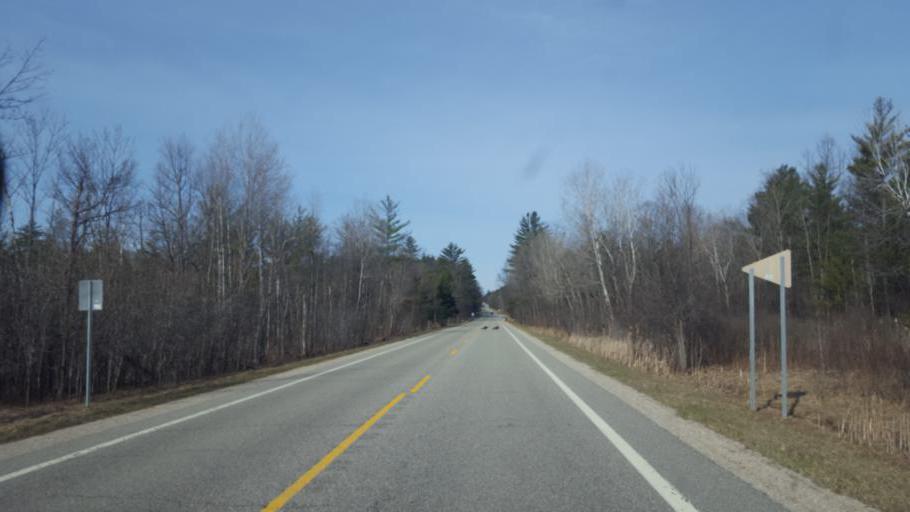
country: US
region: Michigan
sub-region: Newaygo County
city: White Cloud
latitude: 43.5554
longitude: -85.5968
